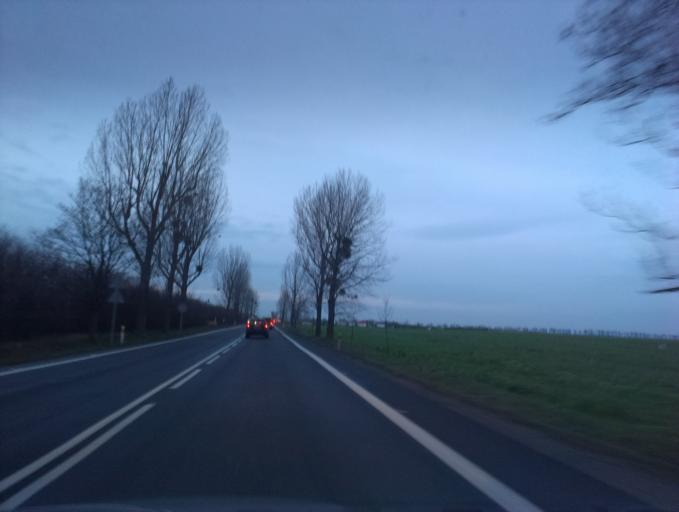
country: PL
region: Greater Poland Voivodeship
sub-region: Powiat obornicki
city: Oborniki
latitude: 52.5829
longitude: 16.8277
